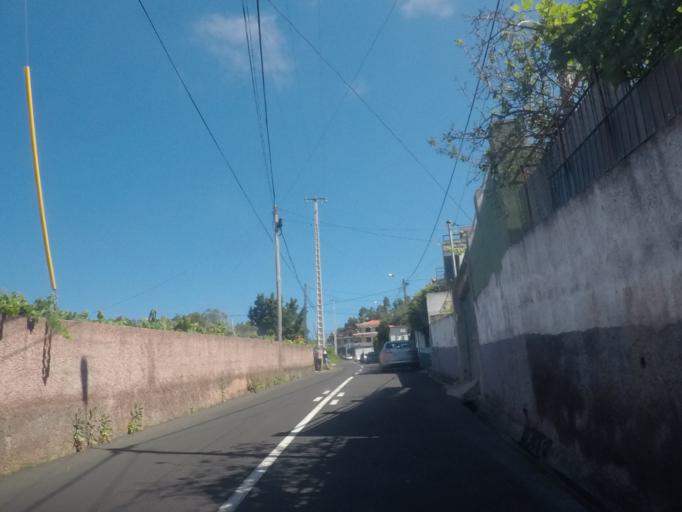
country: PT
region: Madeira
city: Camara de Lobos
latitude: 32.6750
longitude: -16.9648
